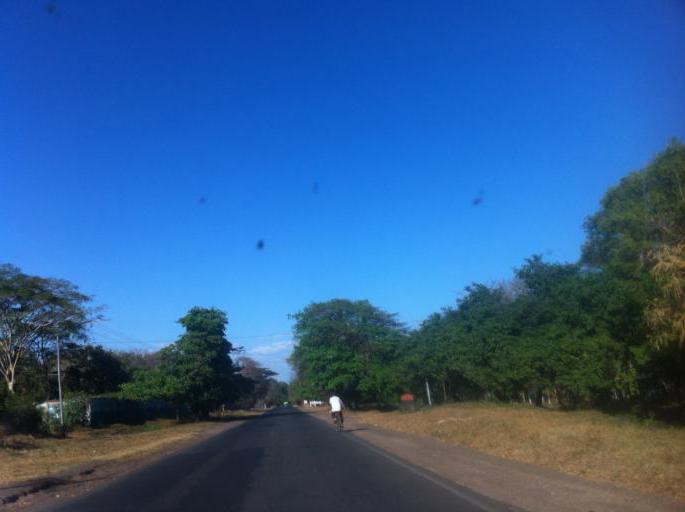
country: NI
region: Granada
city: Granada
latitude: 11.9072
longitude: -85.9809
